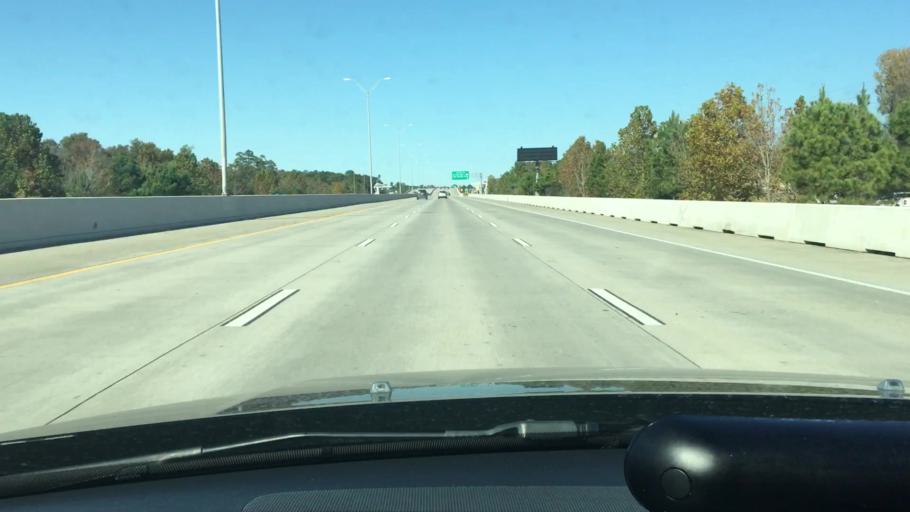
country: US
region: Texas
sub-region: Harris County
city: Sheldon
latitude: 29.8759
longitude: -95.1914
